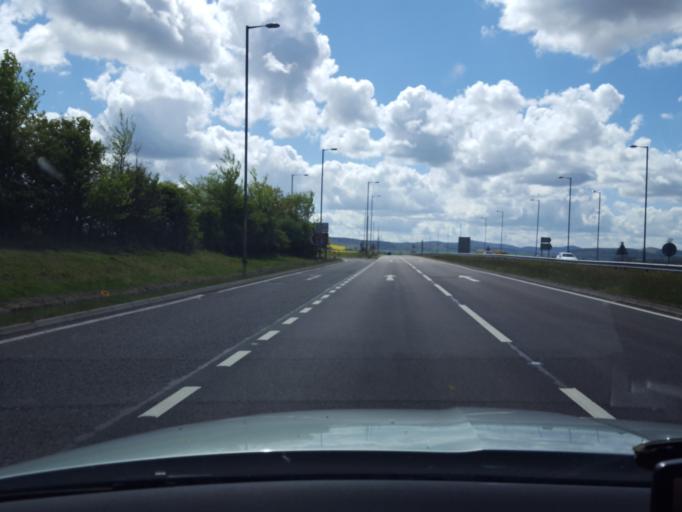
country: GB
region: Scotland
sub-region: Angus
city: Forfar
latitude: 56.6535
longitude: -2.9197
